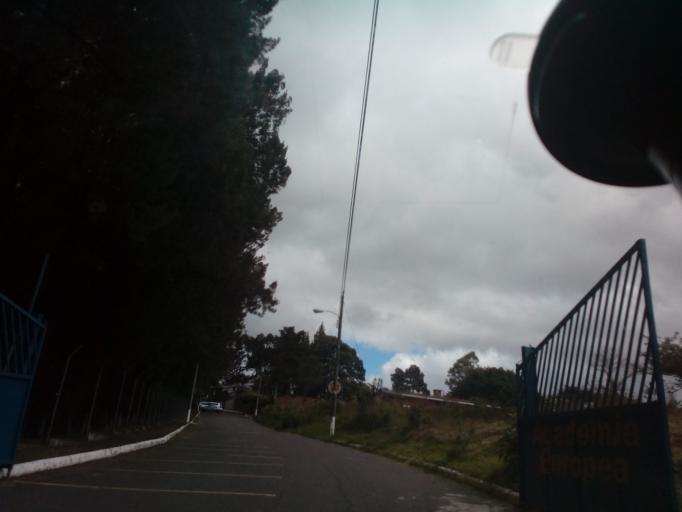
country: GT
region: Guatemala
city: Mixco
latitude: 14.6111
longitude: -90.5942
